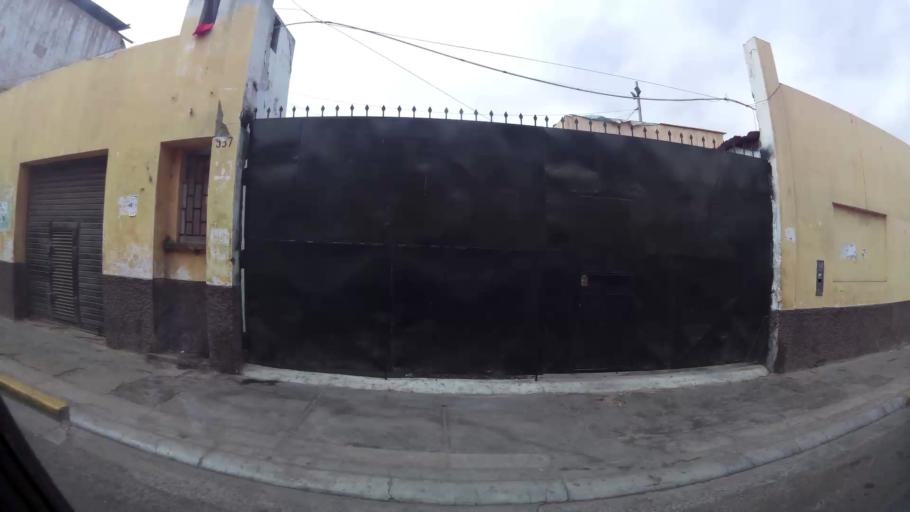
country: PE
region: La Libertad
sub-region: Provincia de Trujillo
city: Trujillo
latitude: -8.1079
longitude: -79.0237
